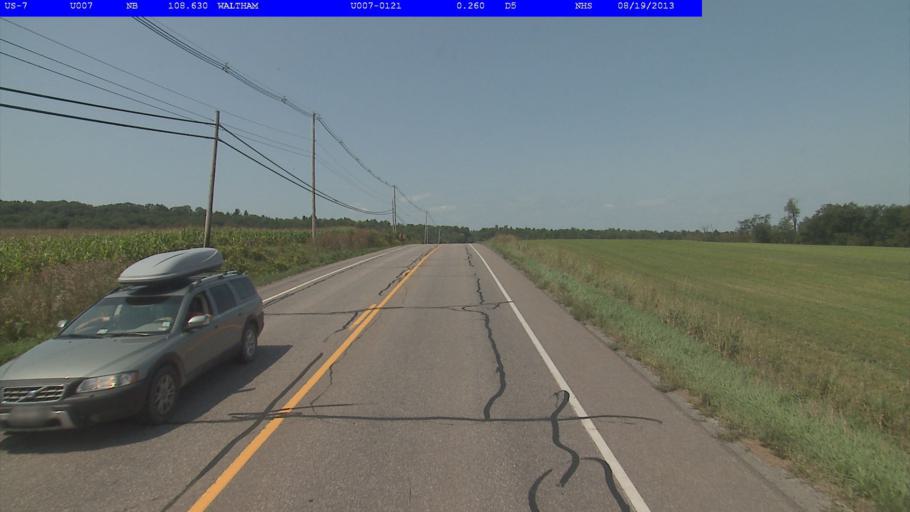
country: US
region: Vermont
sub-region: Addison County
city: Vergennes
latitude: 44.1504
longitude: -73.2137
